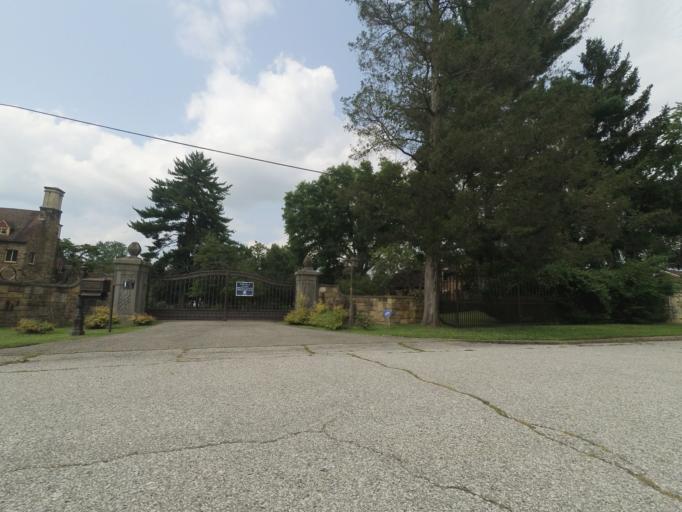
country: US
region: West Virginia
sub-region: Cabell County
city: Huntington
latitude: 38.4044
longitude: -82.4112
